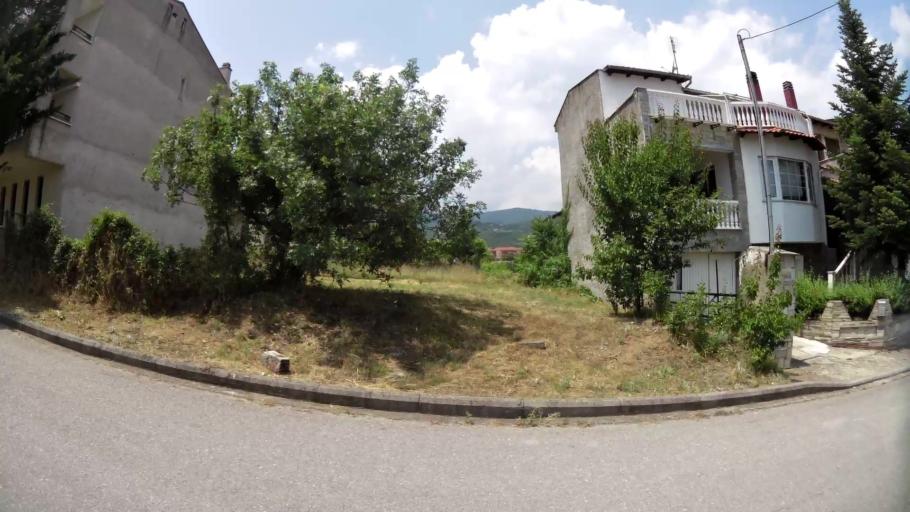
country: GR
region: Central Macedonia
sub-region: Nomos Imathias
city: Veroia
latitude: 40.5127
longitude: 22.1816
